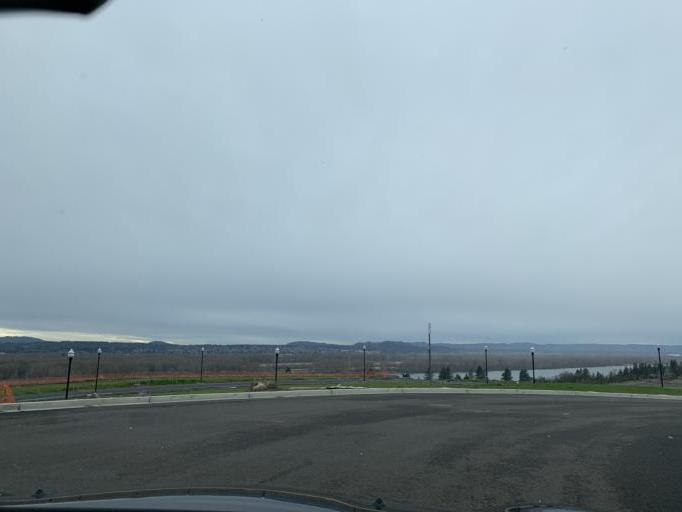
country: US
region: Oregon
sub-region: Multnomah County
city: Fairview
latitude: 45.5861
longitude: -122.4682
